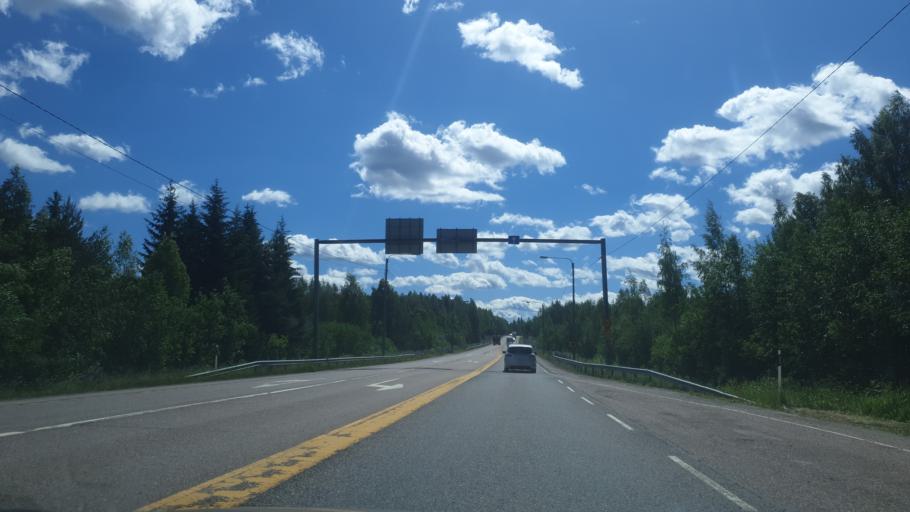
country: FI
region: Northern Savo
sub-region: Varkaus
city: Varkaus
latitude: 62.3513
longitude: 27.8171
